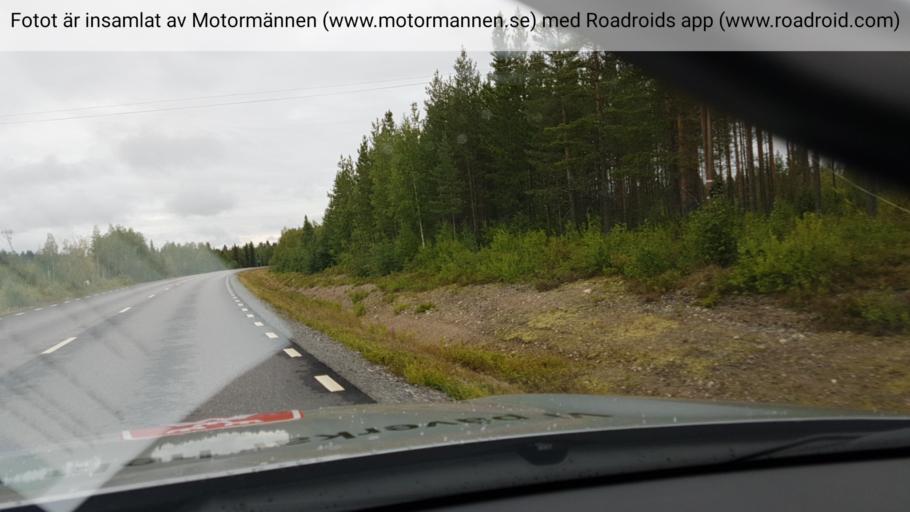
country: SE
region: Norrbotten
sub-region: Alvsbyns Kommun
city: AElvsbyn
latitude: 66.2783
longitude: 20.8243
